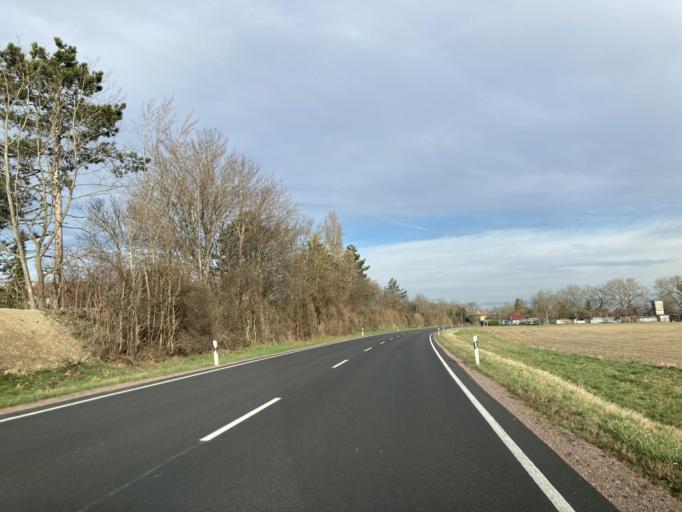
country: DE
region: Baden-Wuerttemberg
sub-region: Freiburg Region
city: Breisach am Rhein
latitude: 48.0392
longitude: 7.5892
